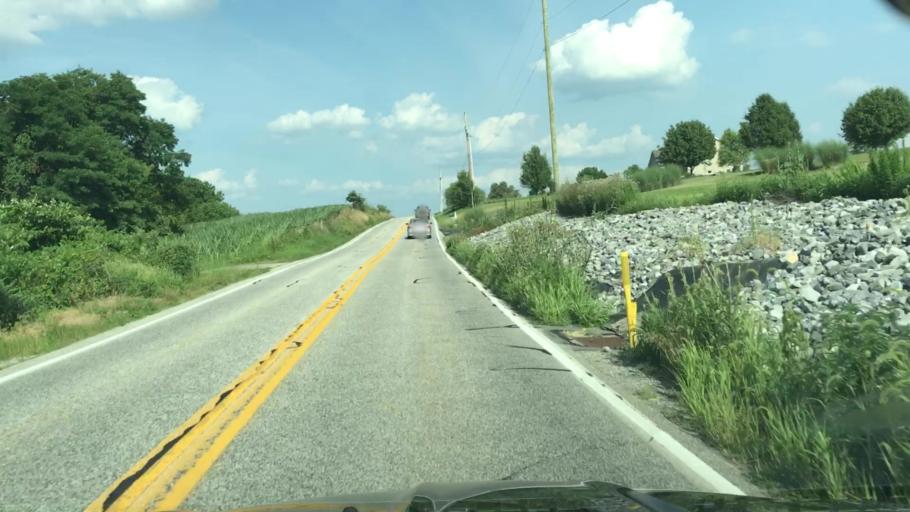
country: US
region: Pennsylvania
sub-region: Cumberland County
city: Boiling Springs
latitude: 40.1804
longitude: -77.0925
